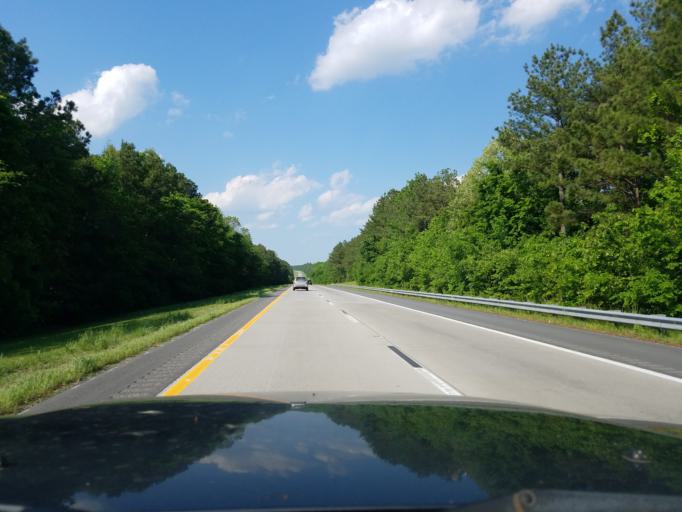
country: US
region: North Carolina
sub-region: Granville County
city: Creedmoor
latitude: 36.1781
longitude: -78.6992
